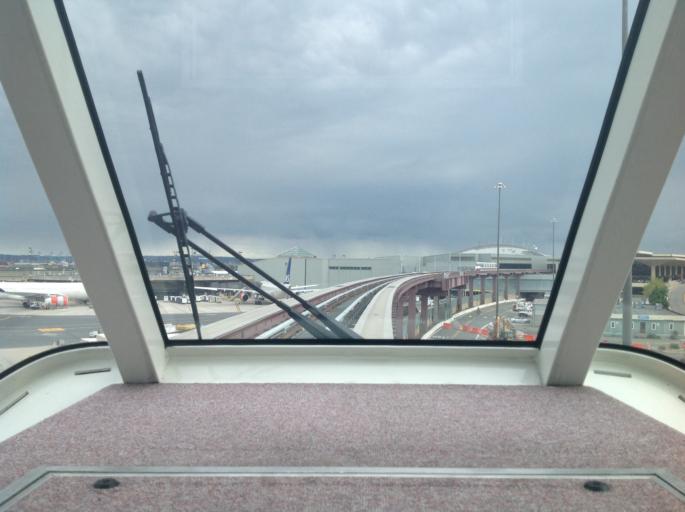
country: US
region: New Jersey
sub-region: Essex County
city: Newark
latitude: 40.6945
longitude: -74.1761
